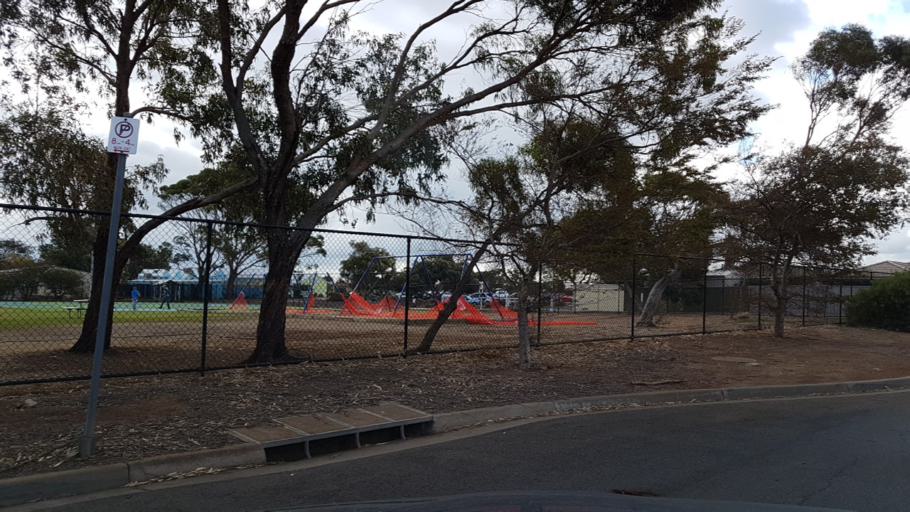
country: AU
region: South Australia
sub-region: Onkaparinga
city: Seaford
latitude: -35.1916
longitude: 138.4760
